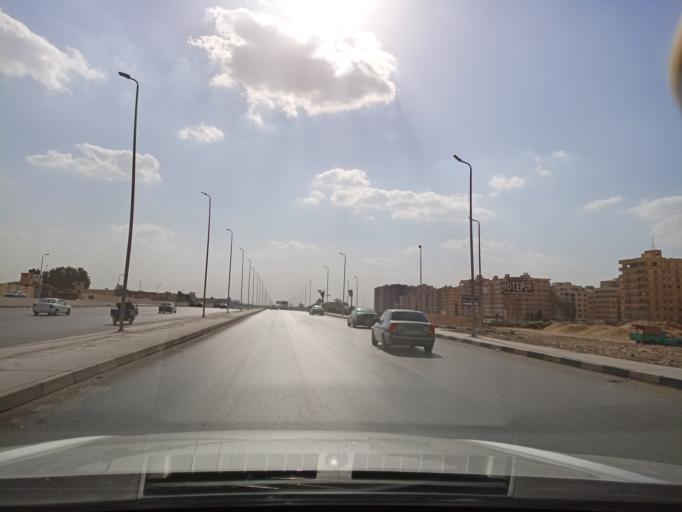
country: EG
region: Muhafazat al Qalyubiyah
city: Al Khankah
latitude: 30.1575
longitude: 31.4544
